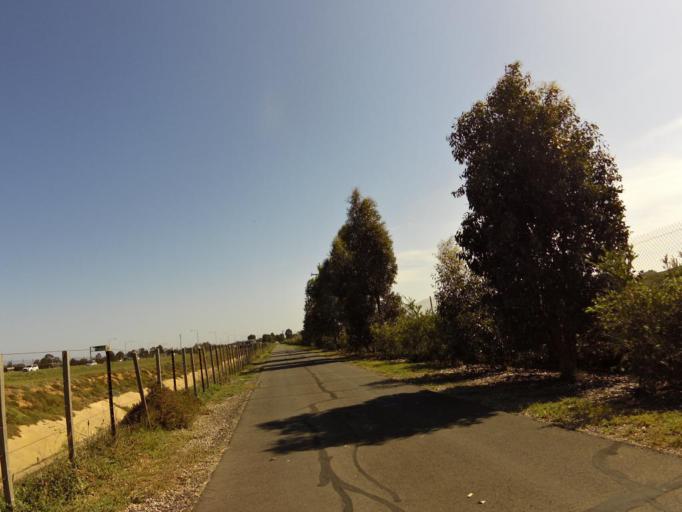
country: AU
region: Victoria
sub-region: Wyndham
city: Werribee
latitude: -37.9084
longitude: 144.6898
